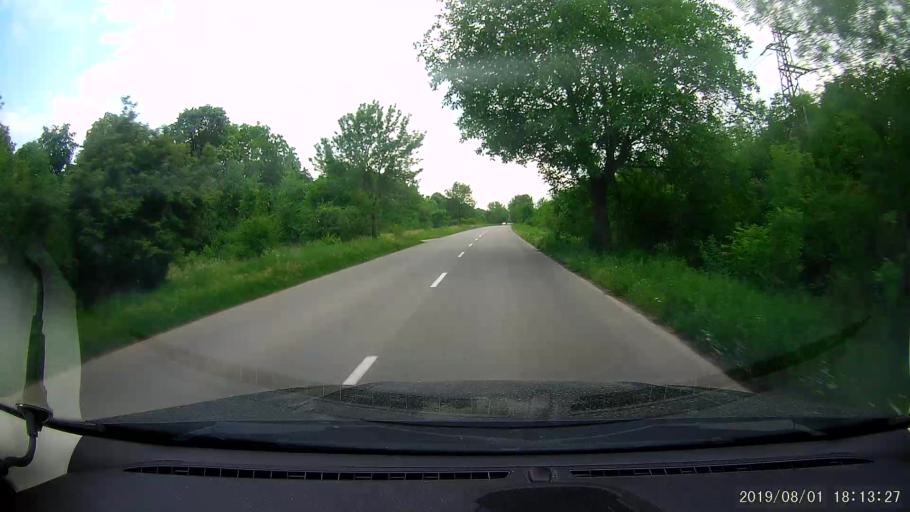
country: BG
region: Silistra
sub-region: Obshtina Dulovo
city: Dulovo
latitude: 43.7890
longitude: 27.1393
